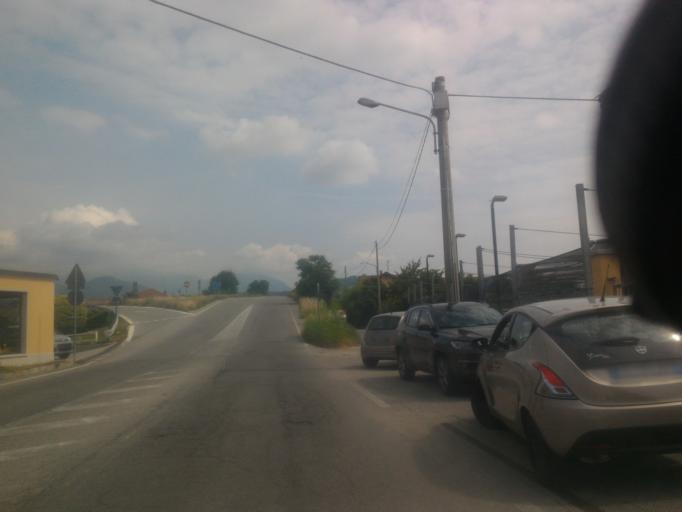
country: IT
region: Piedmont
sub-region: Provincia di Torino
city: San Secondo di Pinerolo
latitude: 44.8776
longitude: 7.3131
